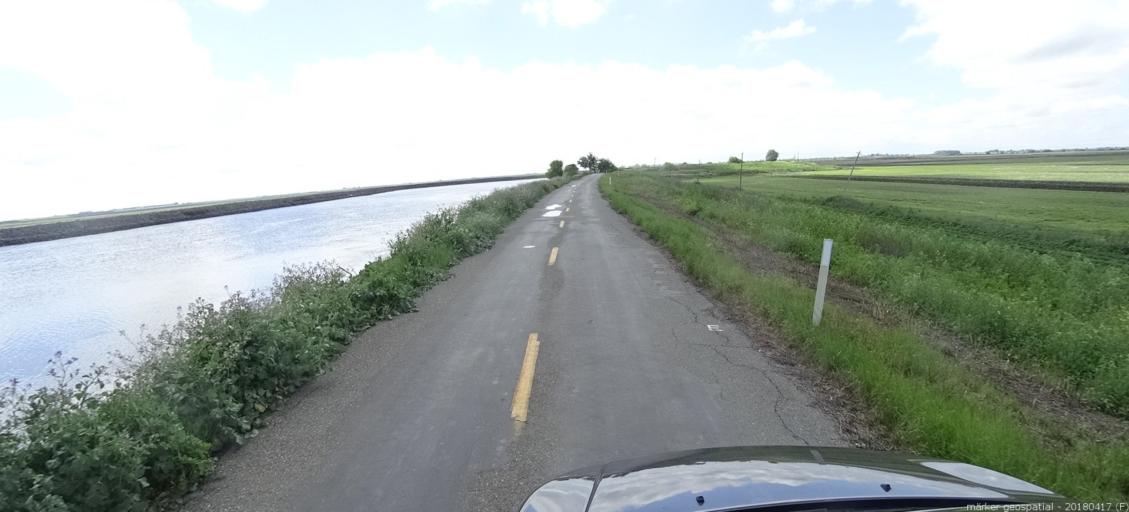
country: US
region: California
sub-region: Sacramento County
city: Walnut Grove
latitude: 38.1670
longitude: -121.5310
